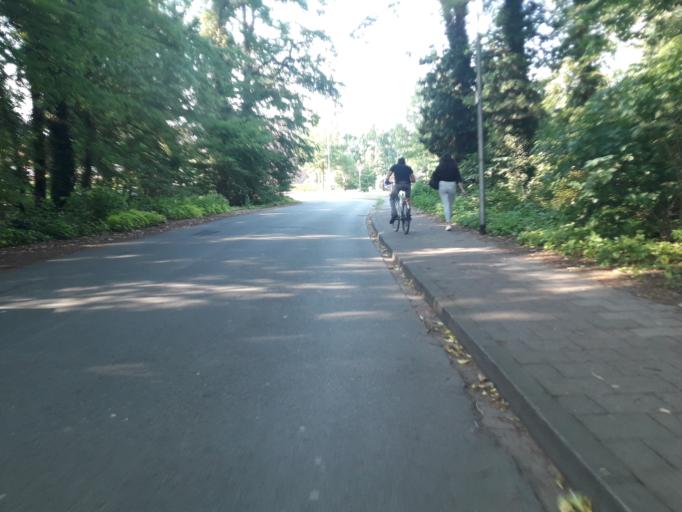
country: DE
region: North Rhine-Westphalia
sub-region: Regierungsbezirk Munster
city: Muenster
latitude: 51.8997
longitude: 7.6347
